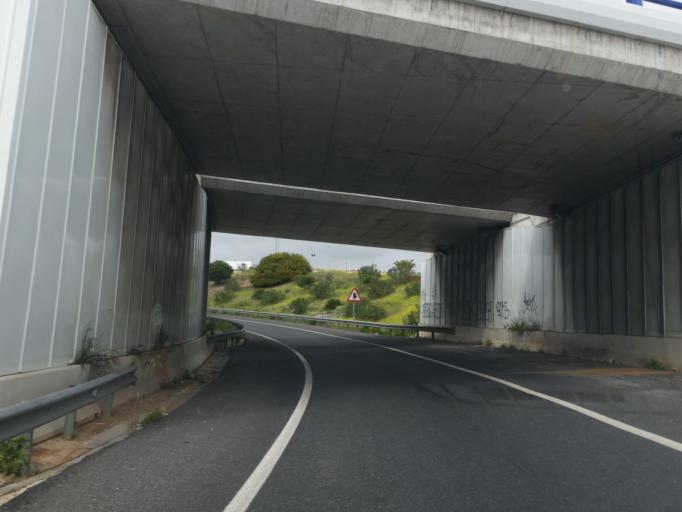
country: ES
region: Andalusia
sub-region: Provincia de Malaga
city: Malaga
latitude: 36.7131
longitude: -4.4563
